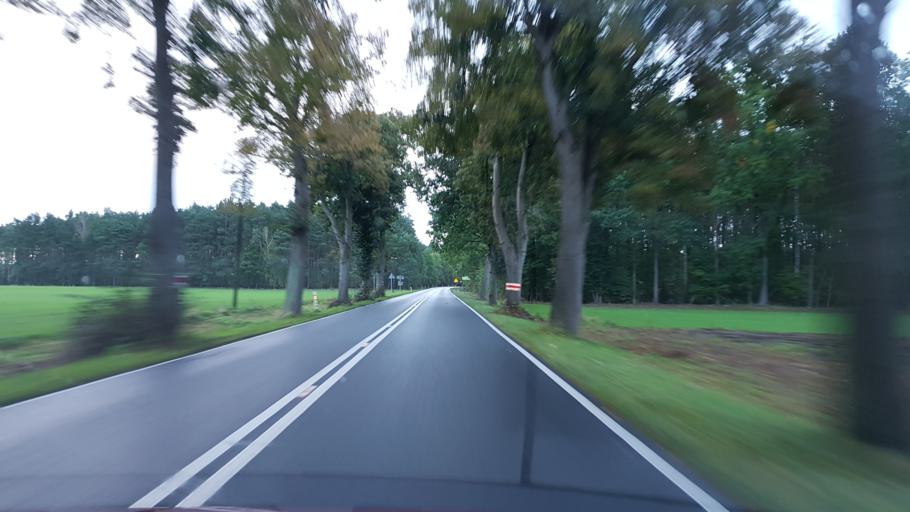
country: PL
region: Greater Poland Voivodeship
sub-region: Powiat zlotowski
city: Krajenka
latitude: 53.2772
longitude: 16.9532
